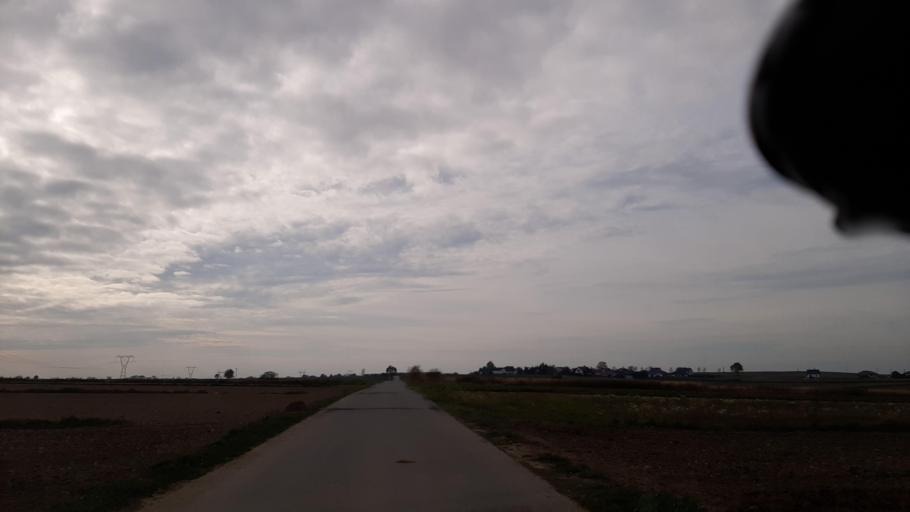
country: PL
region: Lublin Voivodeship
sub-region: Powiat lubelski
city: Garbow
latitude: 51.3842
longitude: 22.3536
